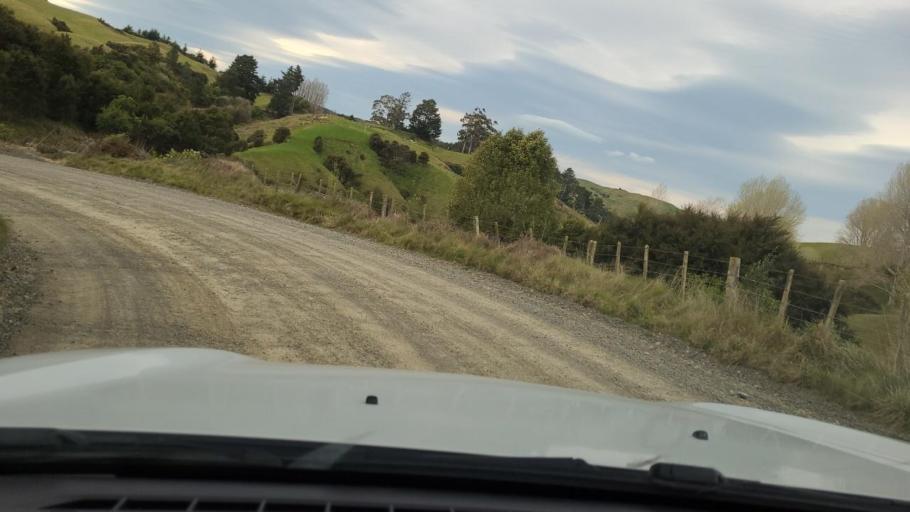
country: NZ
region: Hawke's Bay
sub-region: Napier City
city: Napier
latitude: -39.3027
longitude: 176.8281
